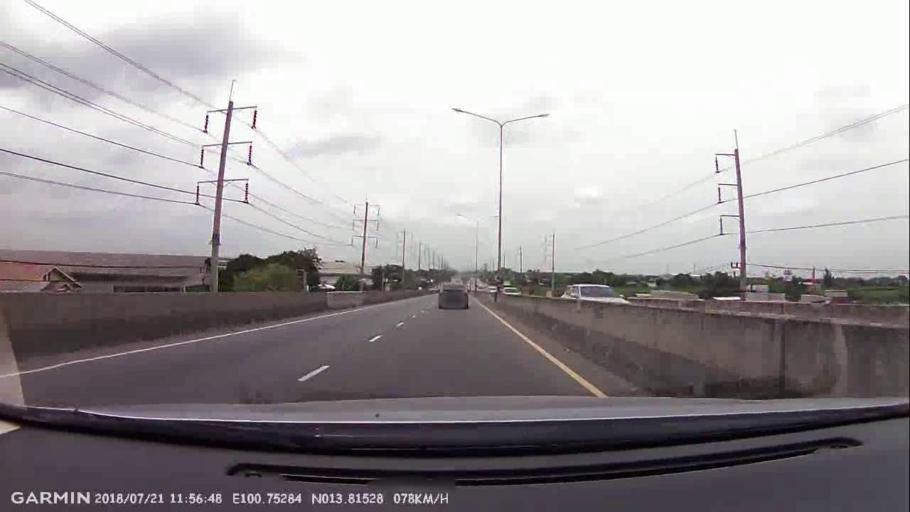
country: TH
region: Bangkok
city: Min Buri
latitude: 13.8150
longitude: 100.7532
